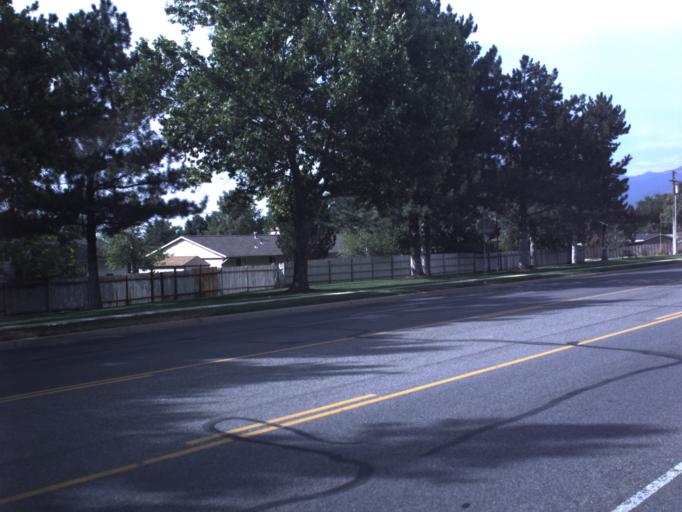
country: US
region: Utah
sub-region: Davis County
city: North Salt Lake
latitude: 40.8509
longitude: -111.9047
